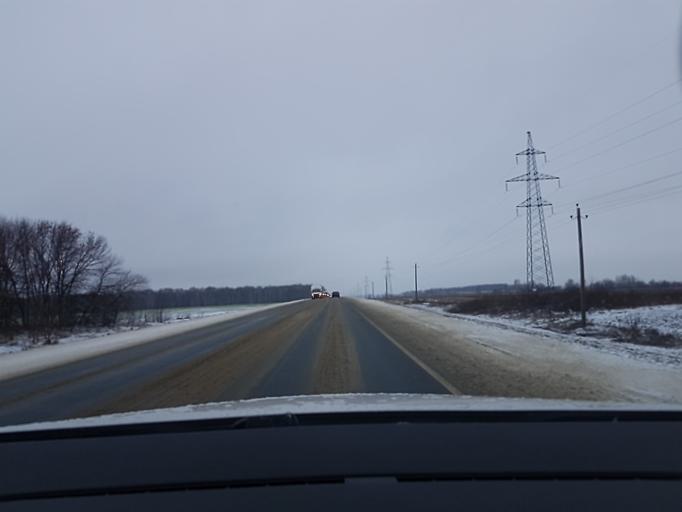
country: RU
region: Rjazan
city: Mikhaylov
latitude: 54.1153
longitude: 39.1915
